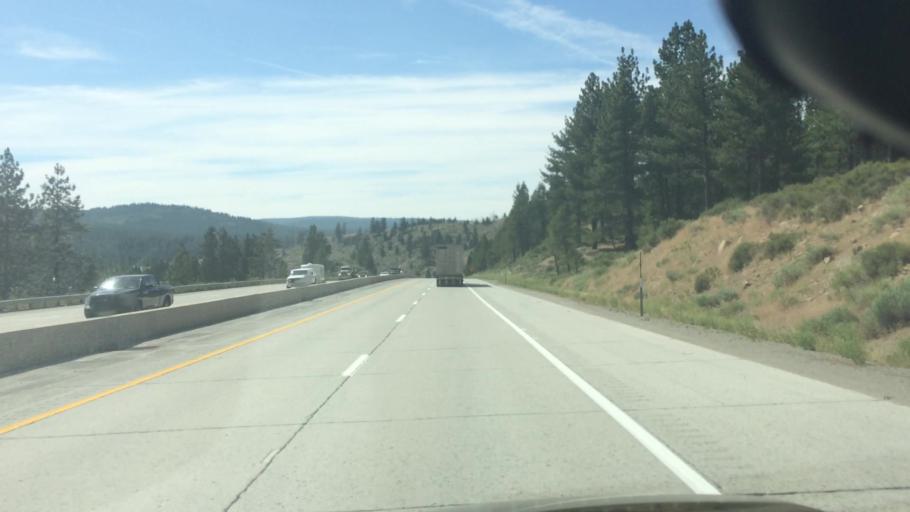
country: US
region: California
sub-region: Nevada County
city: Truckee
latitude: 39.3805
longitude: -120.0740
